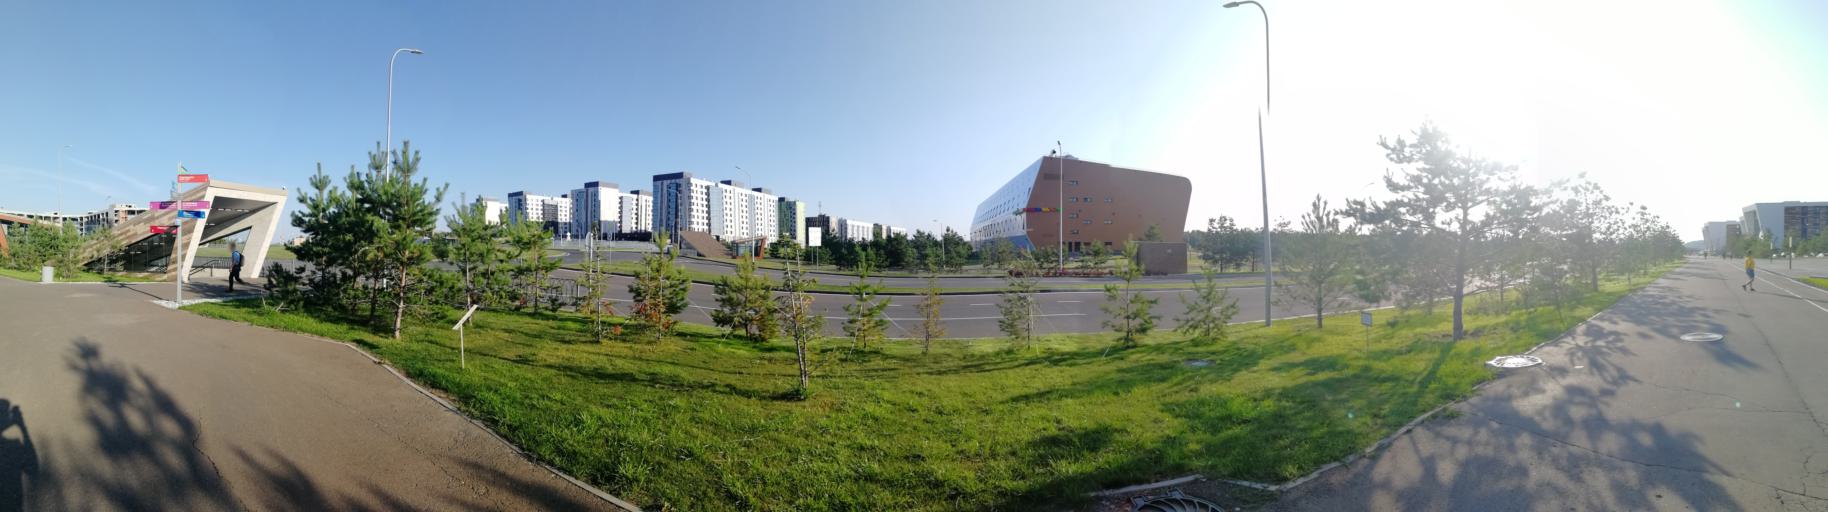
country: RU
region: Tatarstan
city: Sviyazhsk
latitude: 55.7525
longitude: 48.7436
